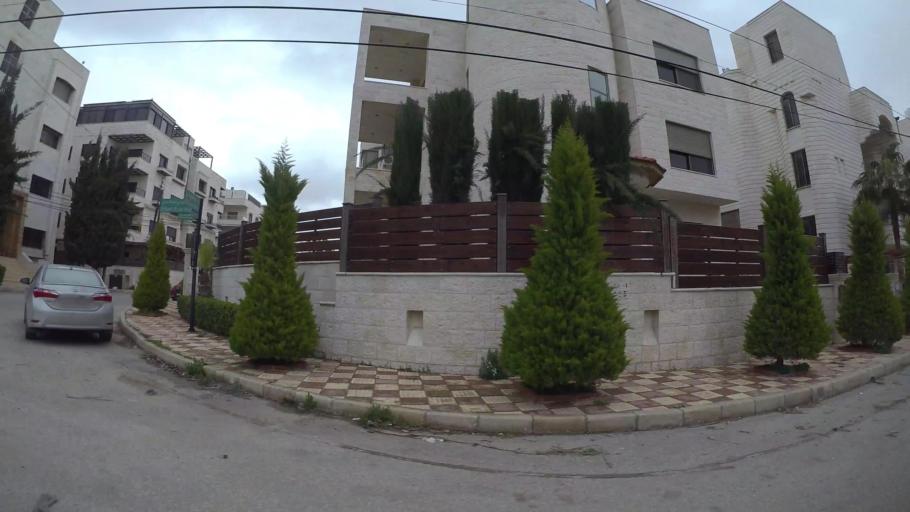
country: JO
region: Amman
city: Wadi as Sir
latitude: 31.9629
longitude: 35.8273
